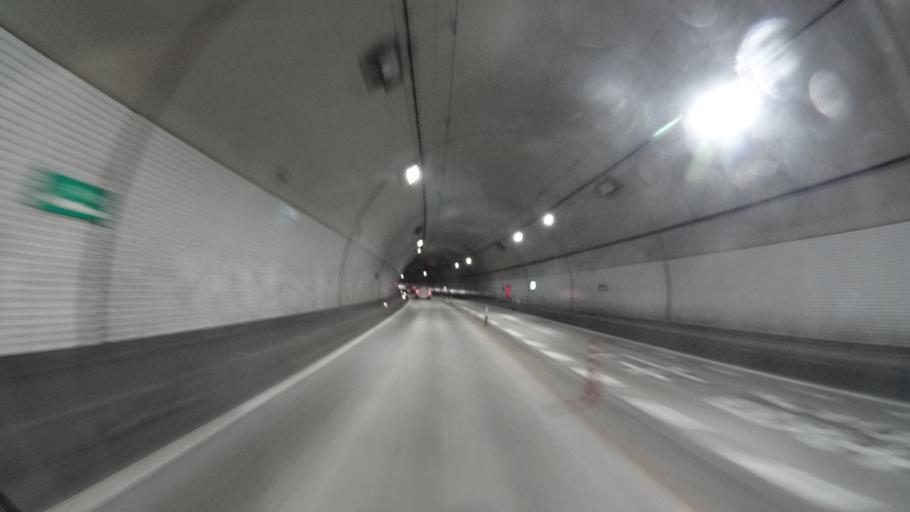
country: JP
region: Gunma
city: Numata
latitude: 36.6595
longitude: 139.1628
